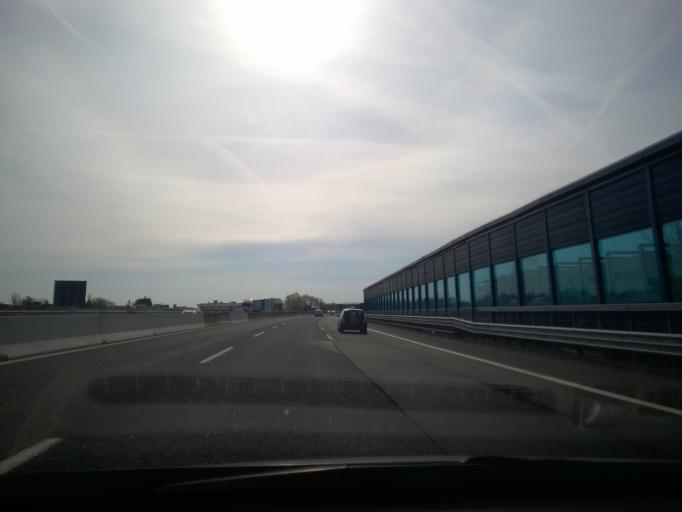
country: IT
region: Emilia-Romagna
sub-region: Forli-Cesena
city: San Mauro Pascoli
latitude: 44.1146
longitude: 12.4154
